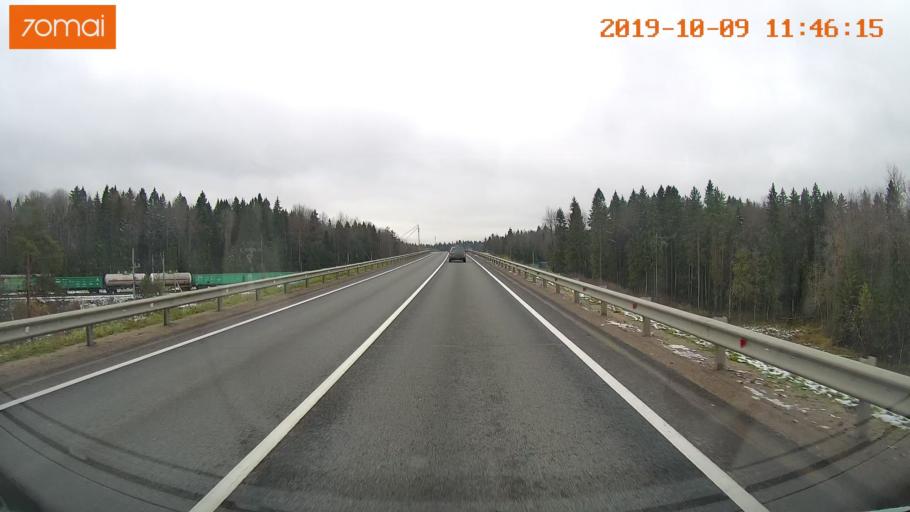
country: RU
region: Vologda
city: Gryazovets
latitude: 58.8560
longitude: 40.2008
